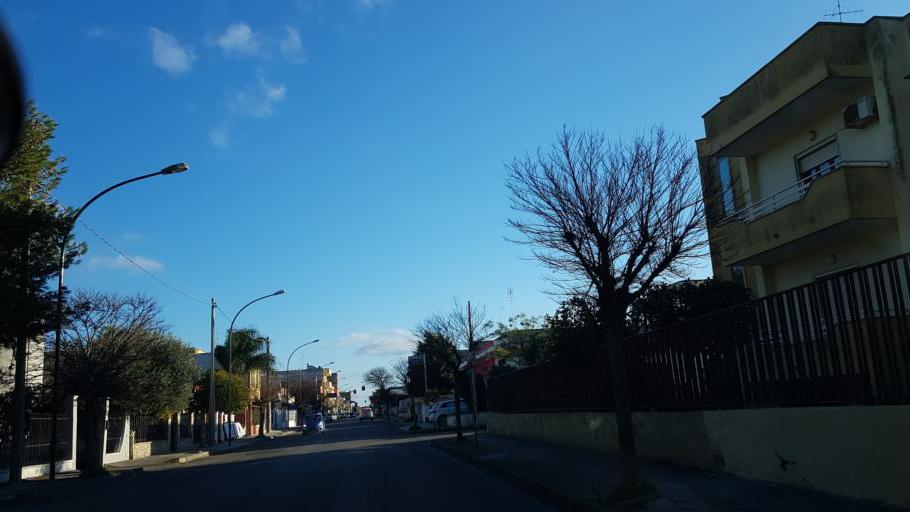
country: IT
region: Apulia
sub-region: Provincia di Lecce
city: Squinzano
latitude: 40.4428
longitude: 18.0346
